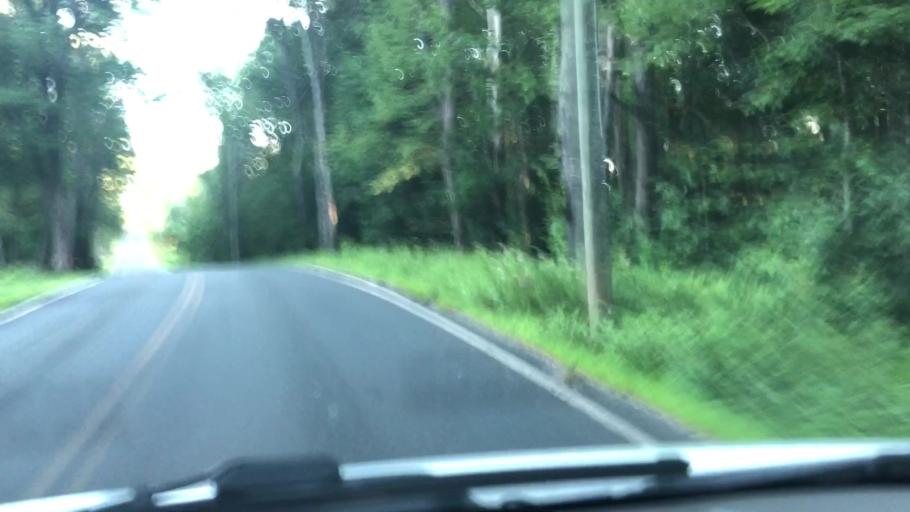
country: US
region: Massachusetts
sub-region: Hampshire County
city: Westhampton
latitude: 42.2834
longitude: -72.7573
